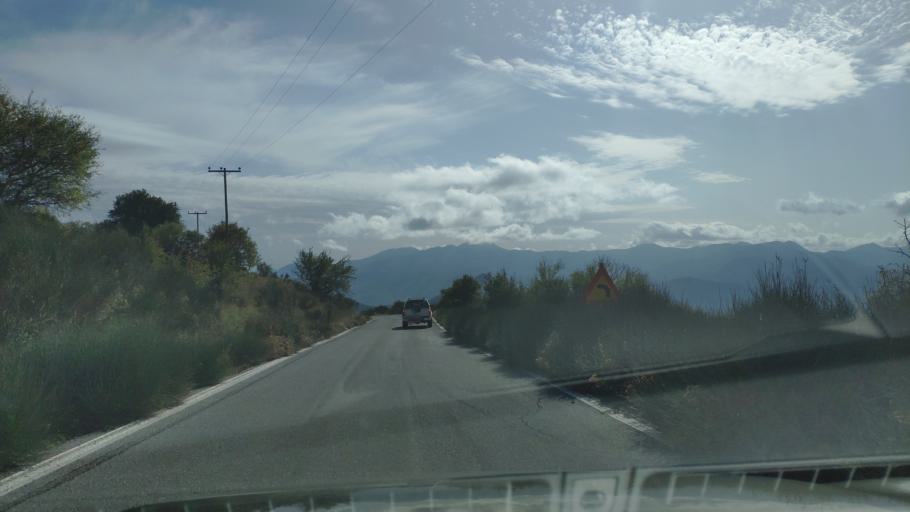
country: GR
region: Peloponnese
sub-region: Nomos Arkadias
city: Dimitsana
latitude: 37.5763
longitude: 22.0185
